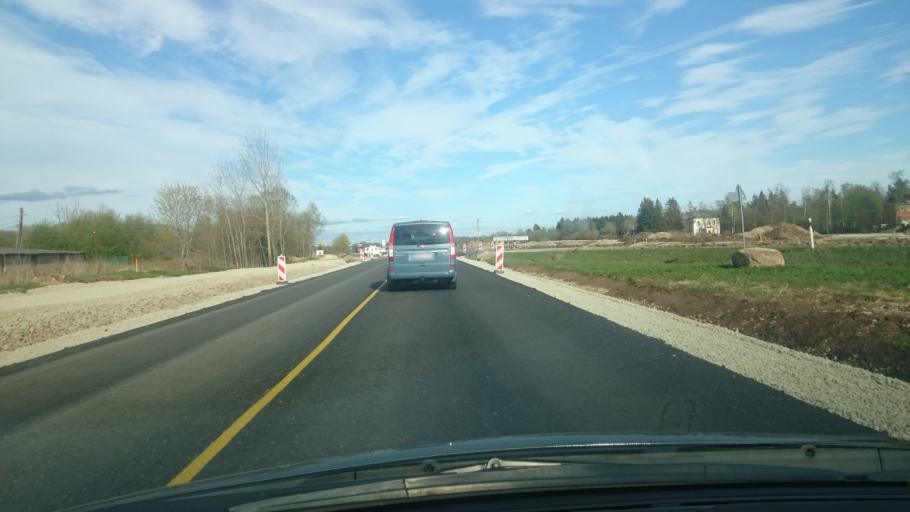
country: EE
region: Ida-Virumaa
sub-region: Sillamaee linn
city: Sillamae
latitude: 59.3915
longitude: 27.7386
